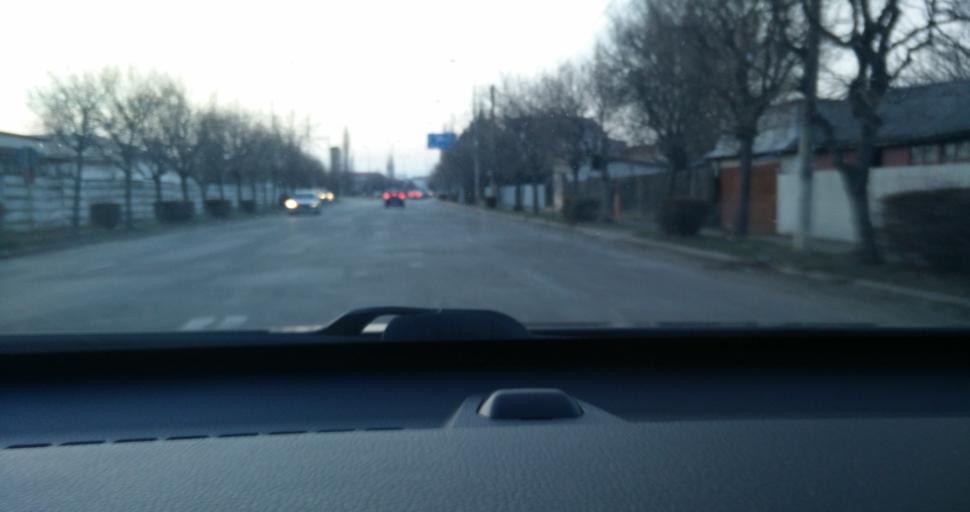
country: RO
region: Vrancea
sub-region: Comuna Vrancioaia
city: Focsani
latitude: 45.6864
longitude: 27.2002
